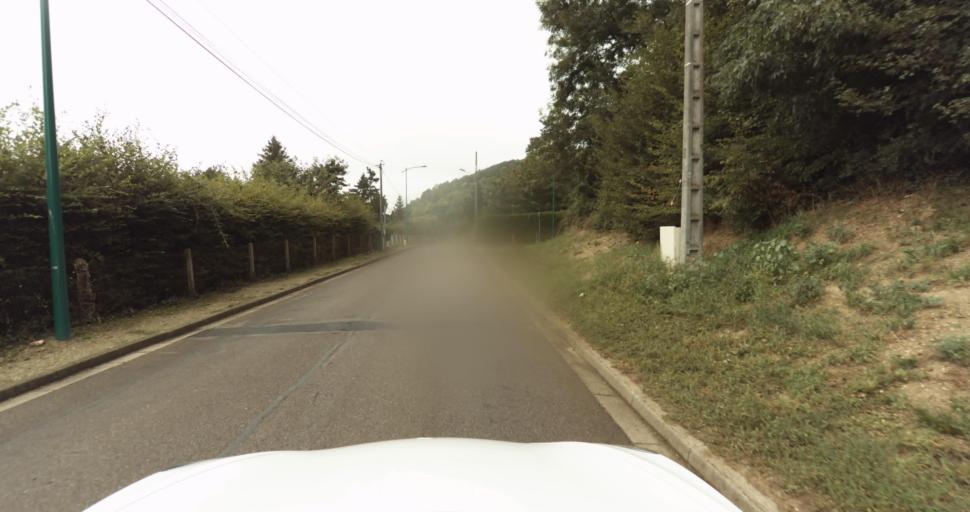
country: FR
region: Haute-Normandie
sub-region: Departement de l'Eure
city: Normanville
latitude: 49.0798
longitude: 1.1586
